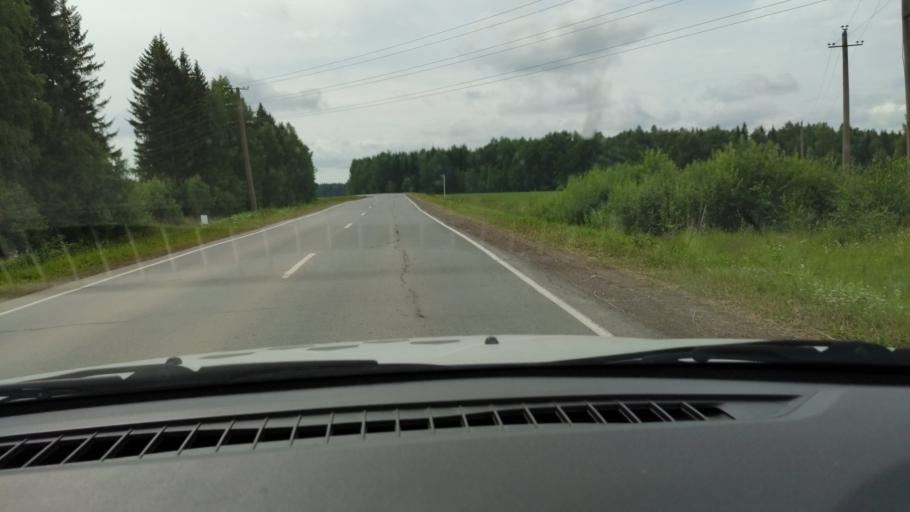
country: RU
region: Perm
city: Kukushtan
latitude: 57.4759
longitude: 56.5754
